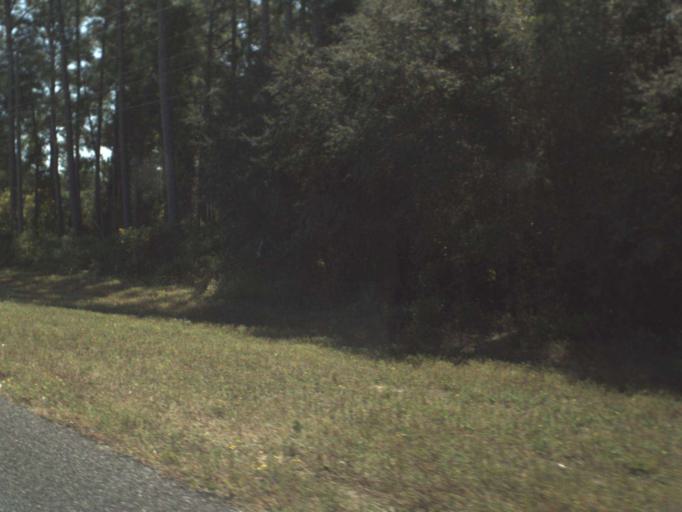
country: US
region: Florida
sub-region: Bay County
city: Laguna Beach
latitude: 30.2568
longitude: -85.9462
